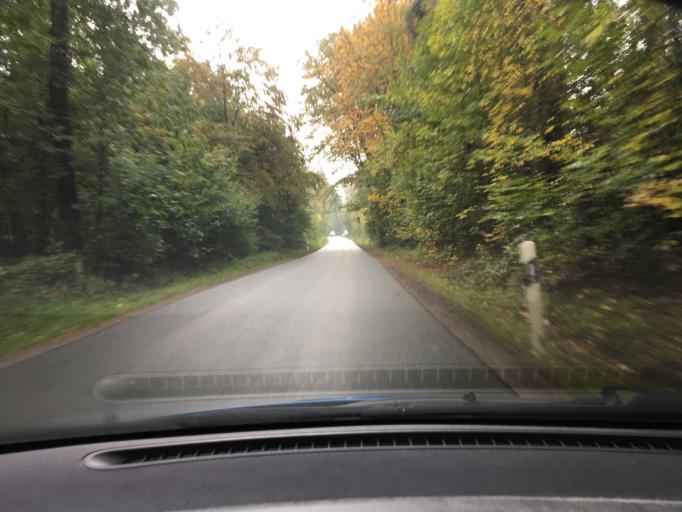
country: DE
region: Schleswig-Holstein
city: Stocksee
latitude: 54.0686
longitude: 10.3626
